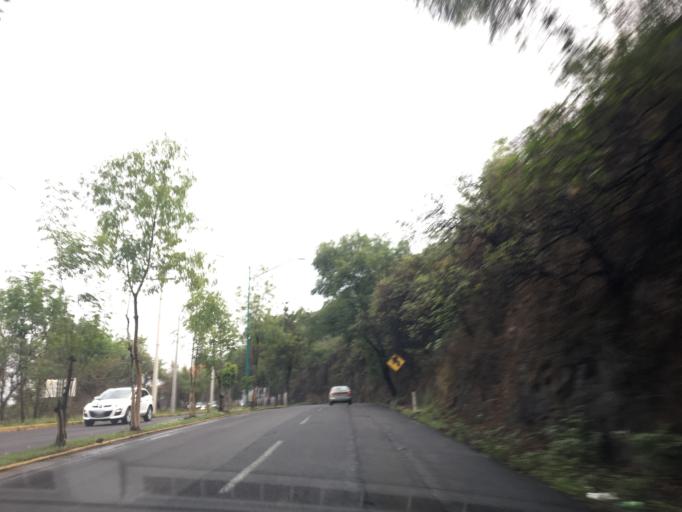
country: MX
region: Mexico
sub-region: Naucalpan de Juarez
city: Rincon Verde
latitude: 19.5336
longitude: -99.2637
